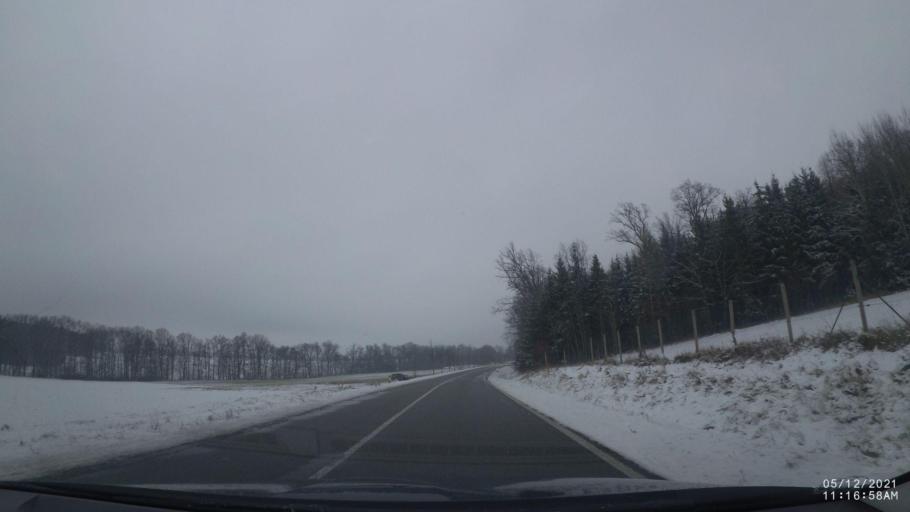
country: CZ
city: Solnice
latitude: 50.1896
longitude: 16.2280
